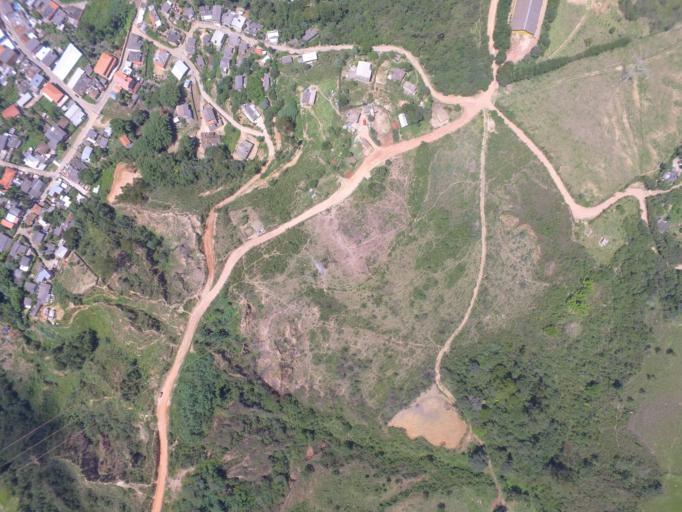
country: BR
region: Minas Gerais
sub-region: Tiradentes
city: Tiradentes
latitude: -21.0503
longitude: -44.0749
